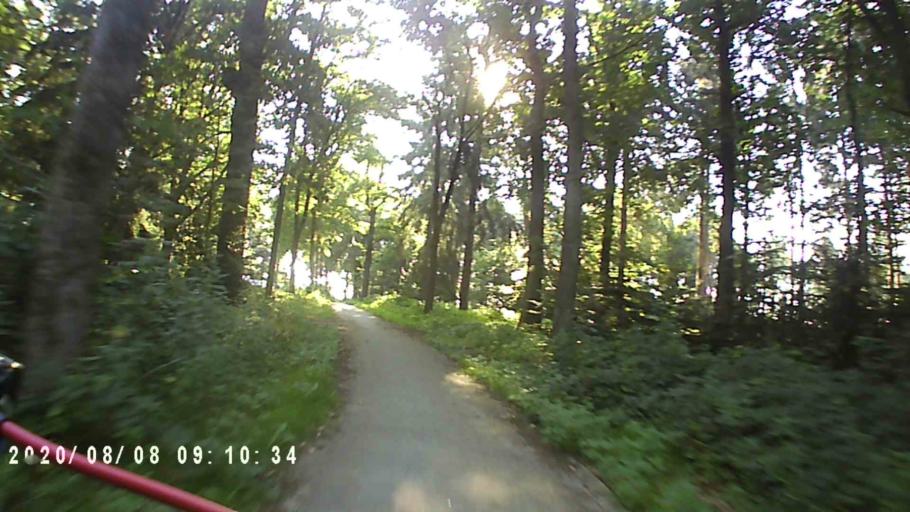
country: NL
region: Groningen
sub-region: Gemeente Leek
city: Leek
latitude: 53.0521
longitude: 6.3267
